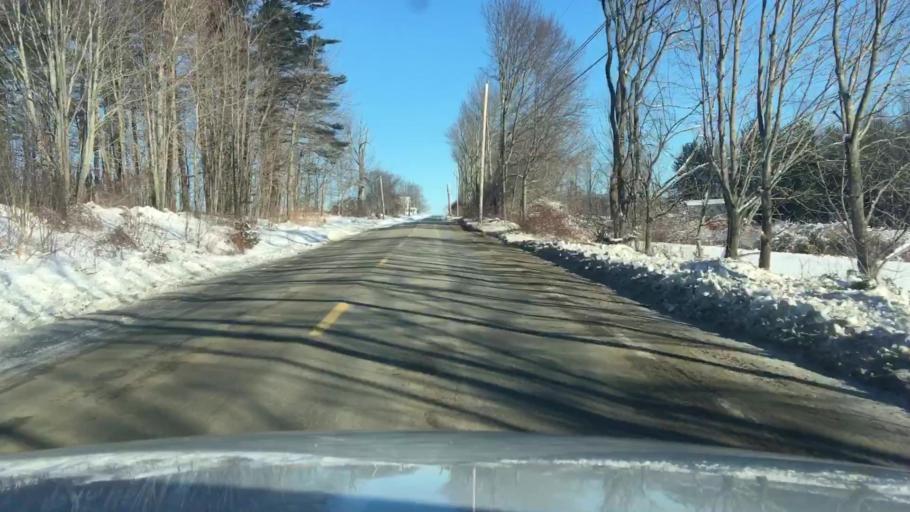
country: US
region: Maine
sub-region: Kennebec County
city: Mount Vernon
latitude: 44.4794
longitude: -69.9725
